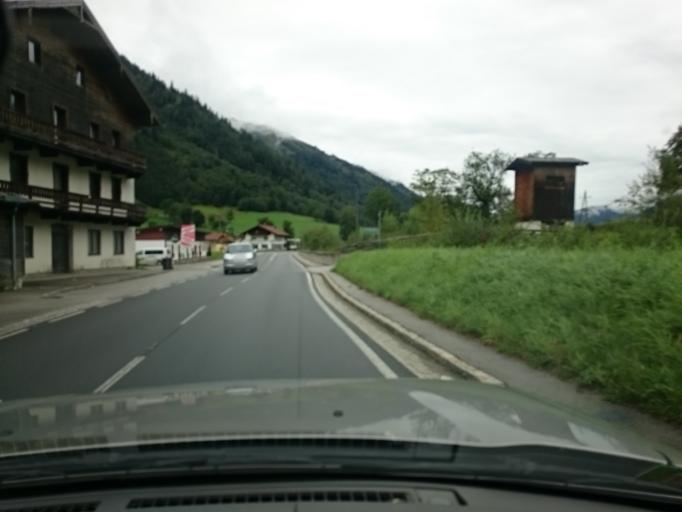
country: AT
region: Salzburg
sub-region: Politischer Bezirk Zell am See
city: Bruck an der Grossglocknerstrasse
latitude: 47.2301
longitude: 12.8269
